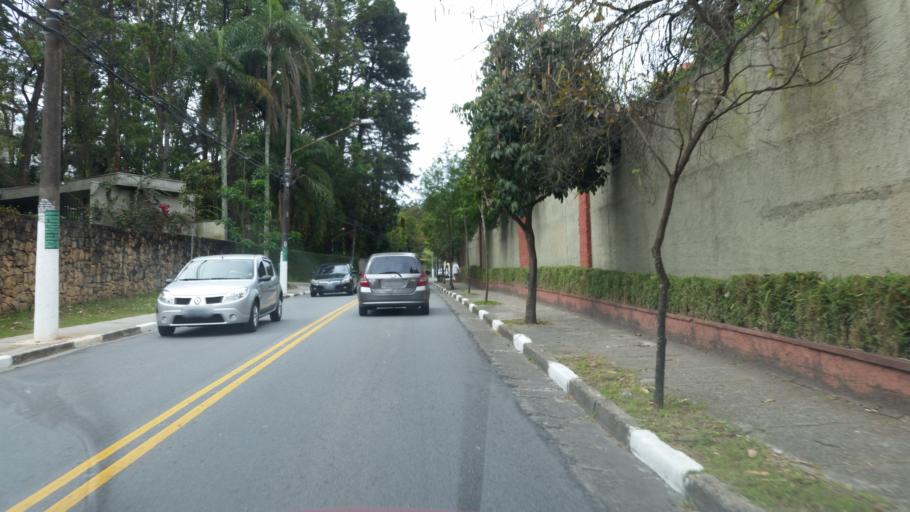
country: BR
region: Sao Paulo
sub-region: Diadema
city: Diadema
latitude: -23.6585
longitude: -46.6840
